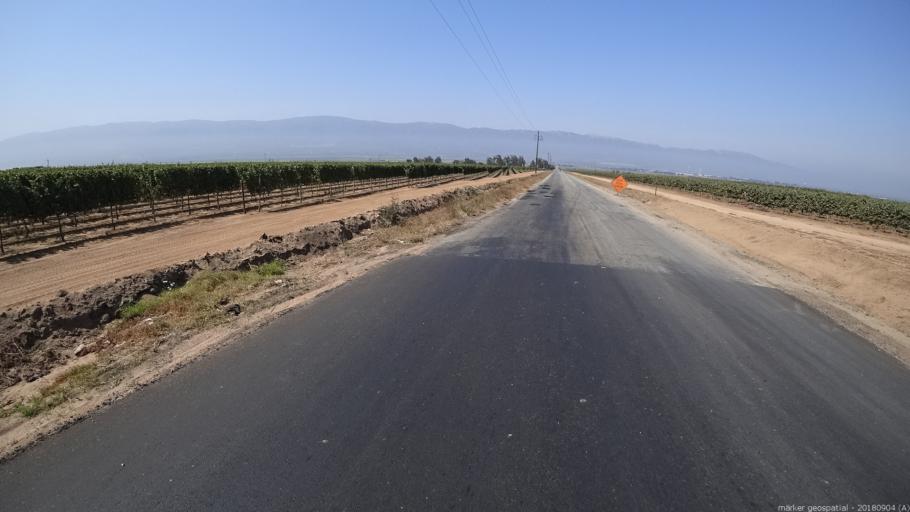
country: US
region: California
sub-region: Monterey County
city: Gonzales
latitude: 36.5007
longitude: -121.3971
